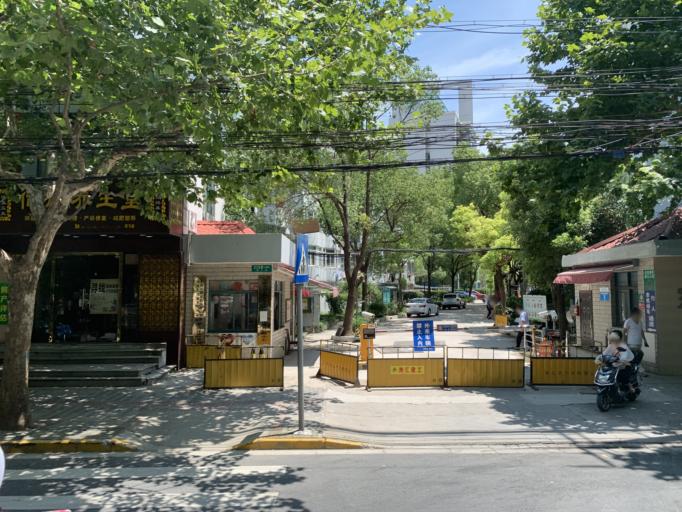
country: CN
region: Shanghai Shi
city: Pudong
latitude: 31.2503
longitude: 121.5589
